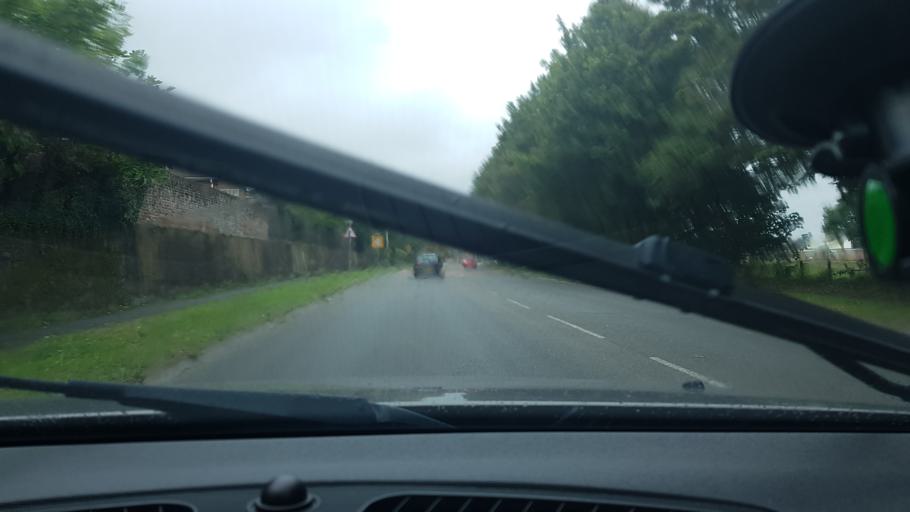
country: GB
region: England
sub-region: West Berkshire
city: Newbury
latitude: 51.4075
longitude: -1.3336
